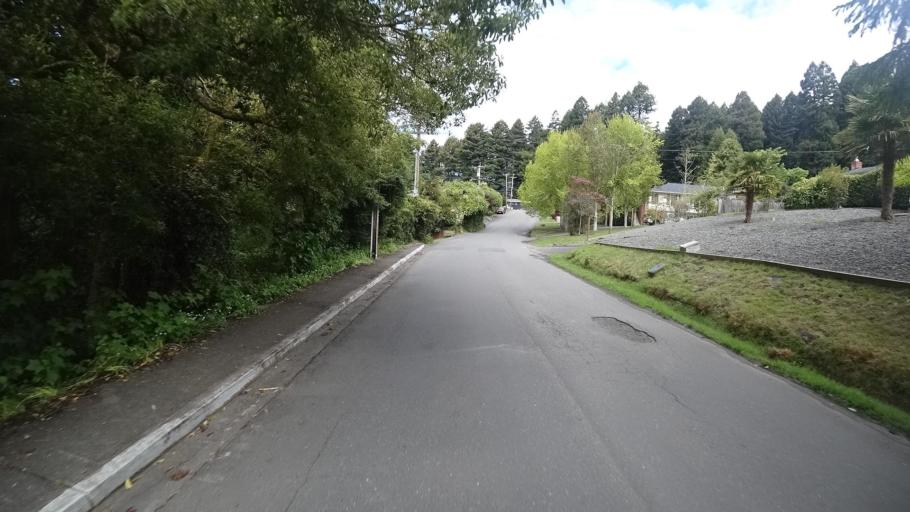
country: US
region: California
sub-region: Humboldt County
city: Arcata
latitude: 40.8671
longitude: -124.0706
